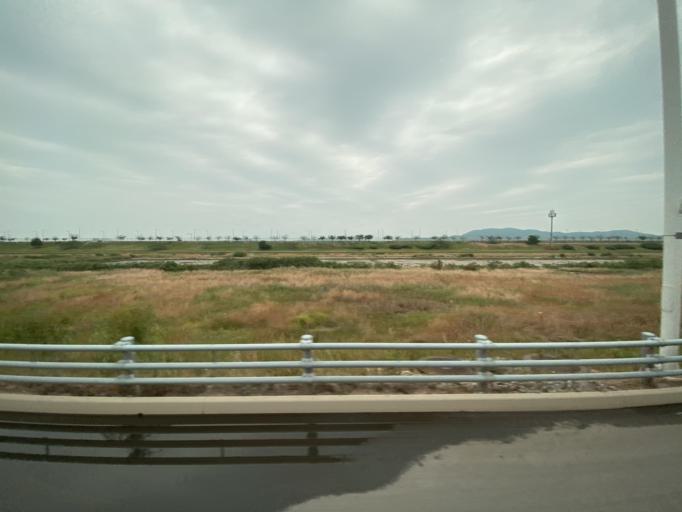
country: KR
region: Incheon
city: Seonwon
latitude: 37.4956
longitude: 126.4273
